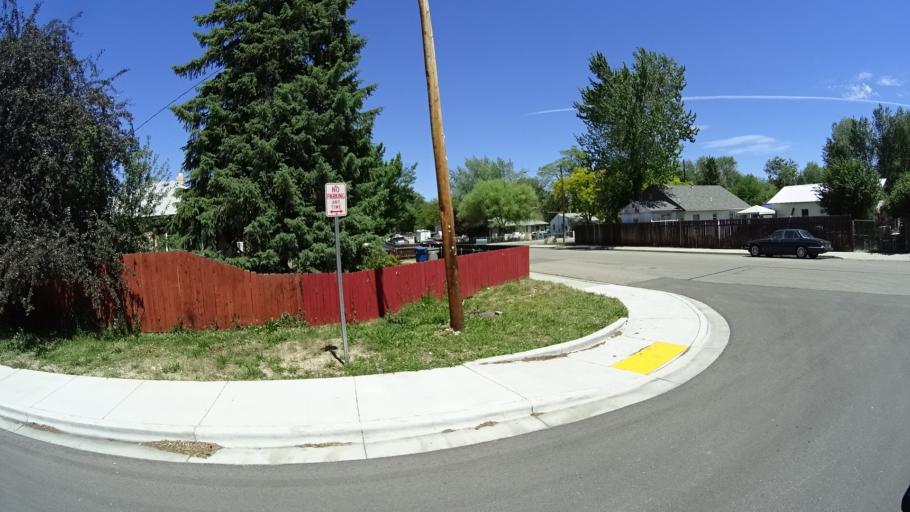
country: US
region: Idaho
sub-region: Ada County
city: Boise
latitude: 43.5825
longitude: -116.2189
